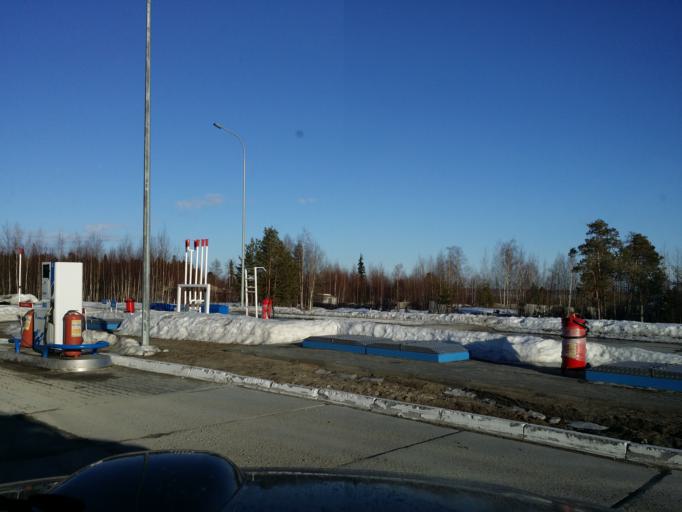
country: RU
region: Khanty-Mansiyskiy Avtonomnyy Okrug
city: Megion
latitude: 61.0652
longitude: 76.2118
